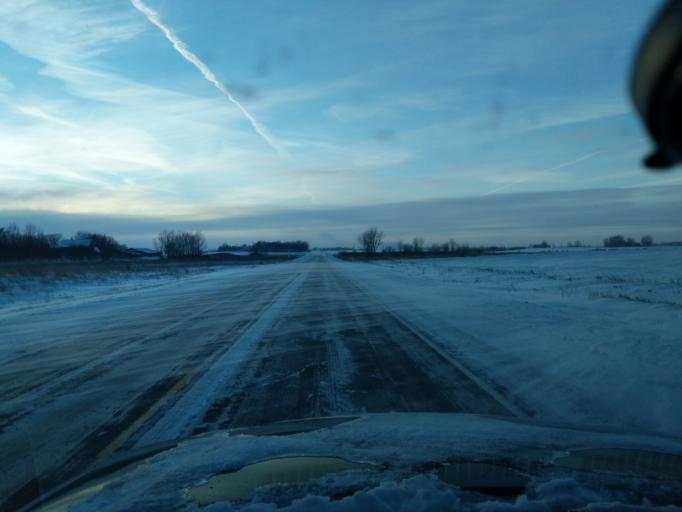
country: US
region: Minnesota
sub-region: Renville County
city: Renville
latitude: 44.7890
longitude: -95.1117
